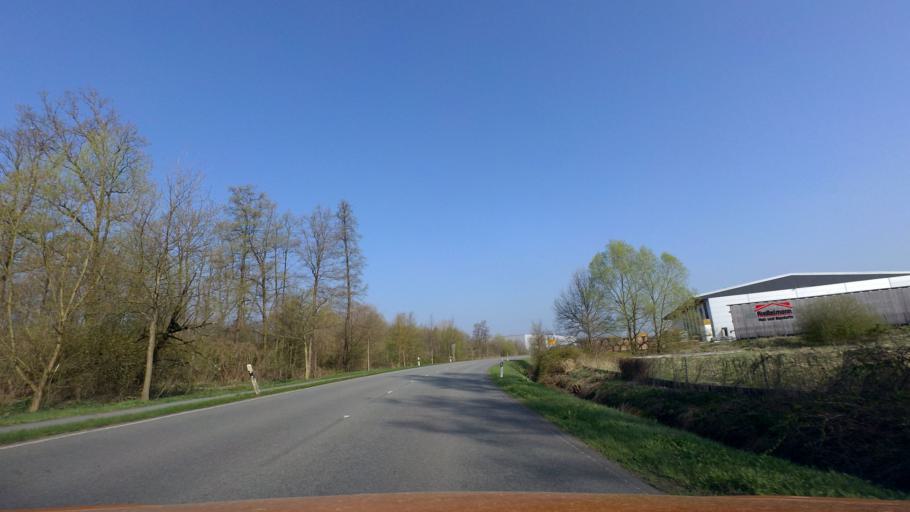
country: DE
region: Lower Saxony
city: Dinklage
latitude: 52.6697
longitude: 8.1378
